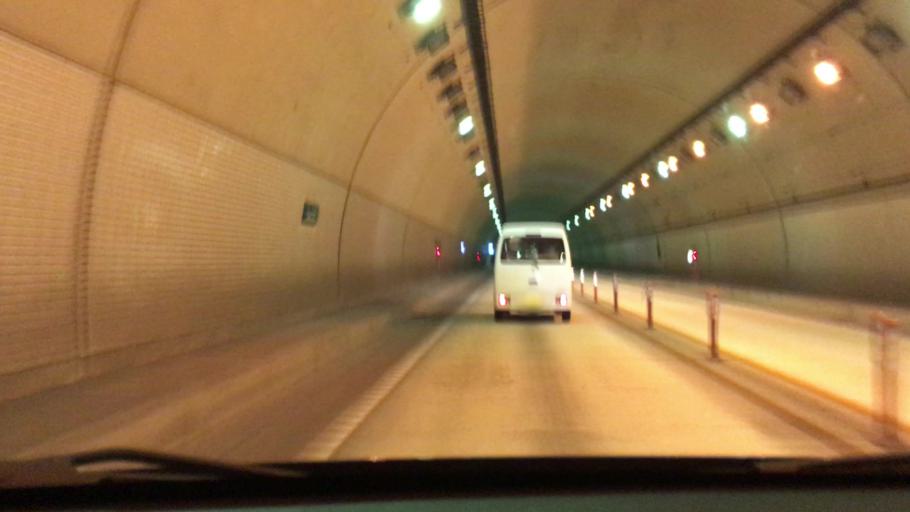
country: JP
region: Nagasaki
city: Sasebo
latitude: 33.0893
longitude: 129.7784
